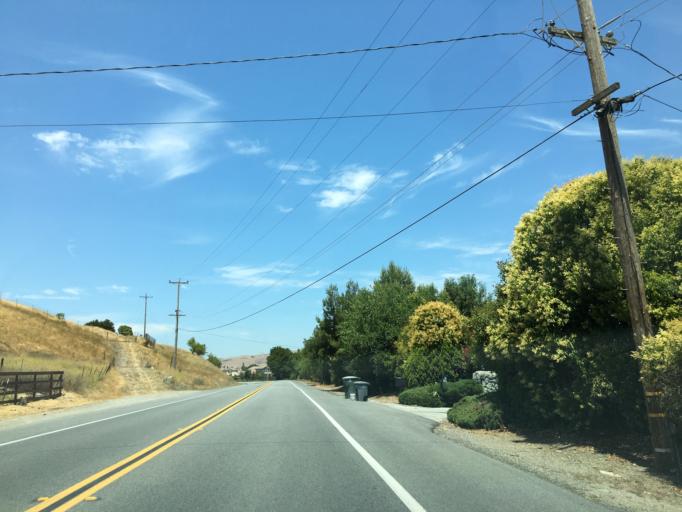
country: US
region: California
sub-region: Santa Clara County
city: Morgan Hill
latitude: 37.1437
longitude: -121.6692
